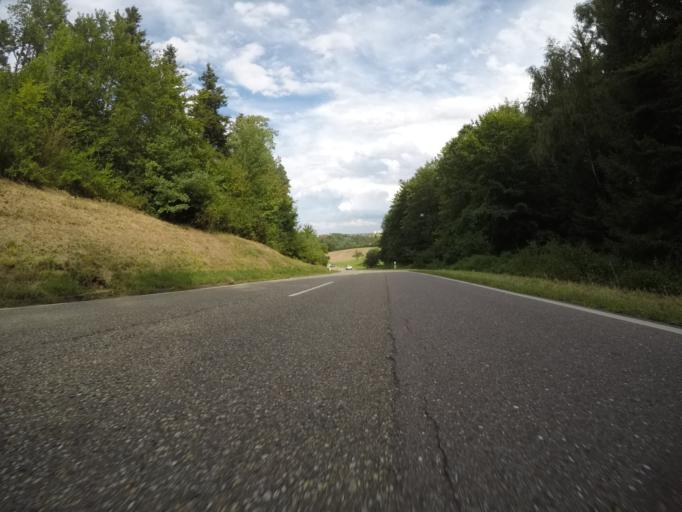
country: DE
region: Baden-Wuerttemberg
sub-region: Karlsruhe Region
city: Horb am Neckar
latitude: 48.4516
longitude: 8.6650
